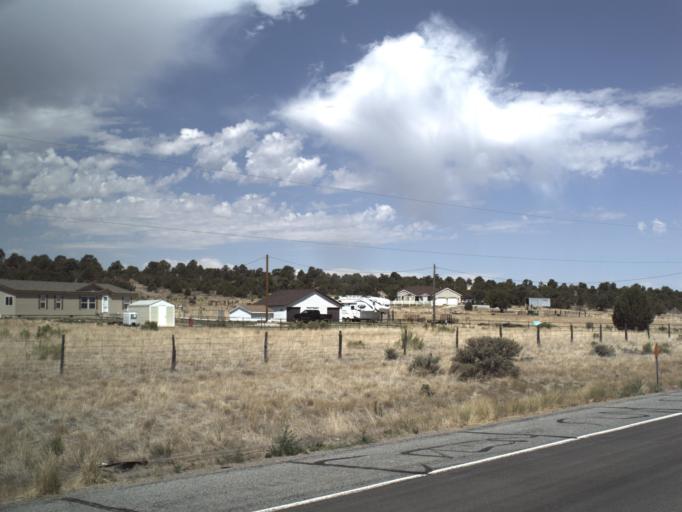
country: US
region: Utah
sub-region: Utah County
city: Eagle Mountain
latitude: 40.0205
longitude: -112.2800
